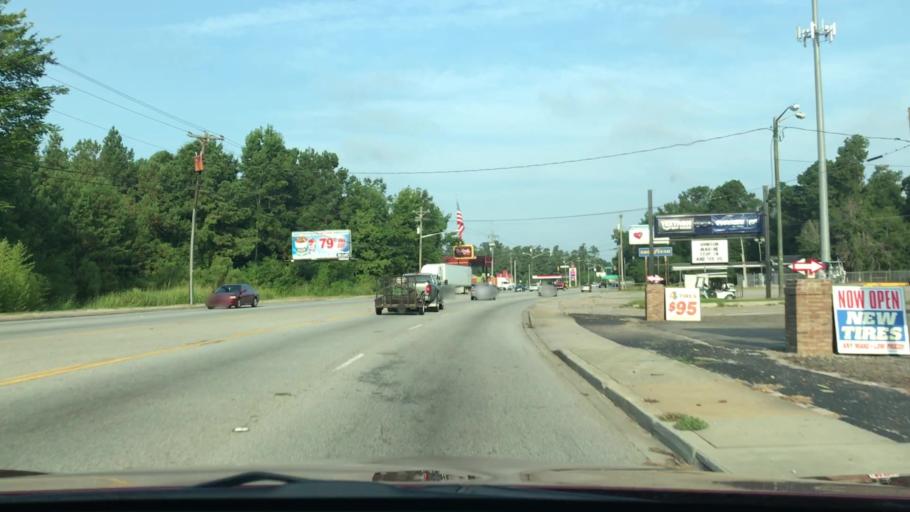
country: US
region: South Carolina
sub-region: Orangeburg County
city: Edisto
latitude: 33.4816
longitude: -80.8784
